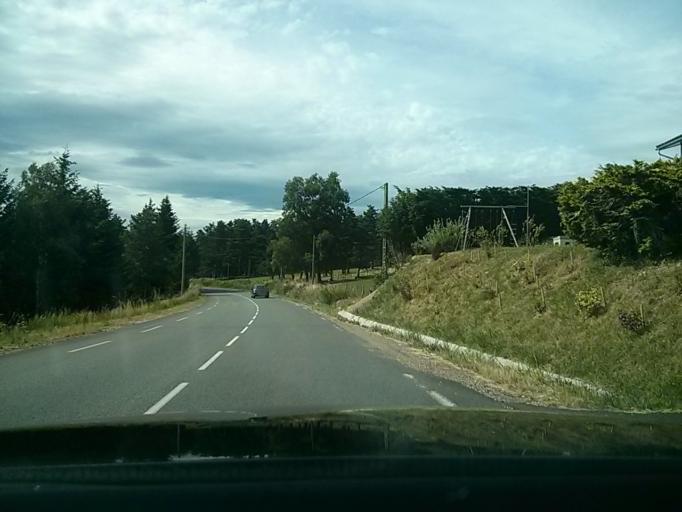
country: FR
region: Rhone-Alpes
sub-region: Departement de la Loire
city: Saint-Genest-Malifaux
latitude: 45.3751
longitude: 4.4951
